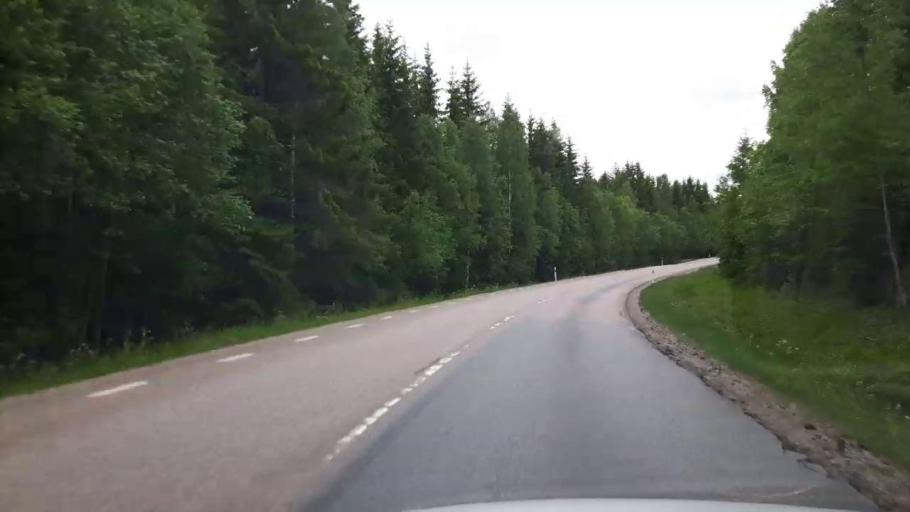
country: SE
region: Dalarna
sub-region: Hedemora Kommun
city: Brunna
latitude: 60.1849
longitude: 15.9996
